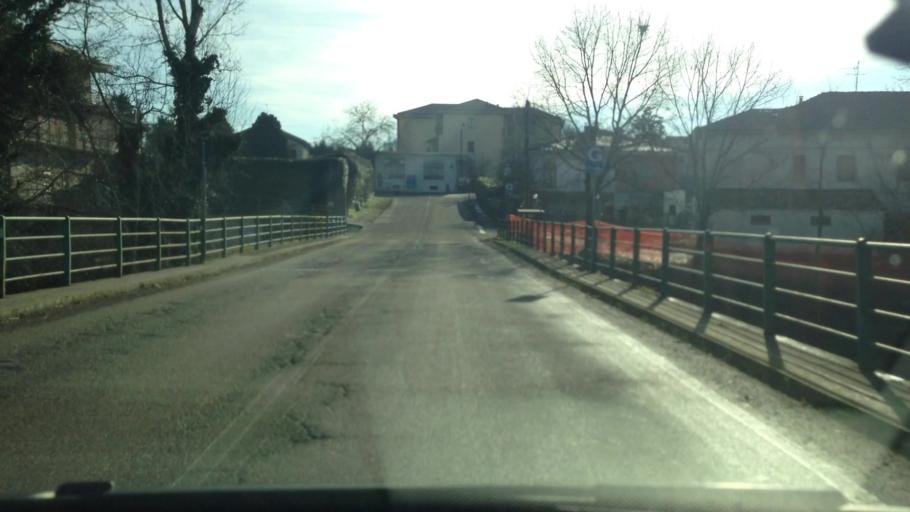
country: IT
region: Piedmont
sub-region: Provincia di Alessandria
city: Masio
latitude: 44.8717
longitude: 8.4106
